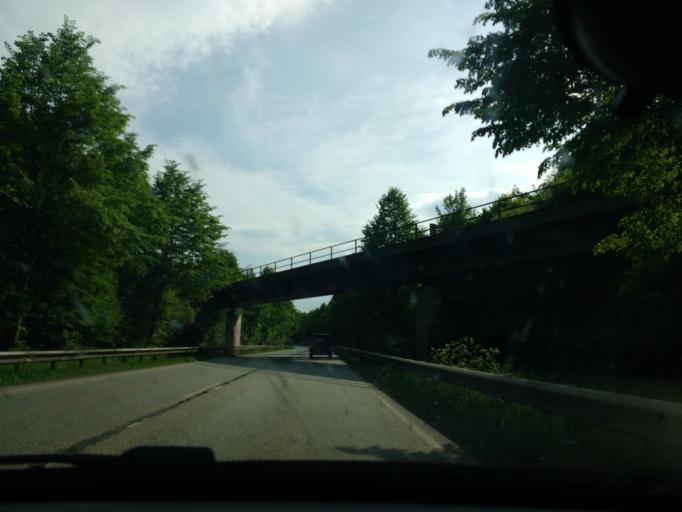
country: DE
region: Schleswig-Holstein
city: Einhaus
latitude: 53.7260
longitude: 10.7366
